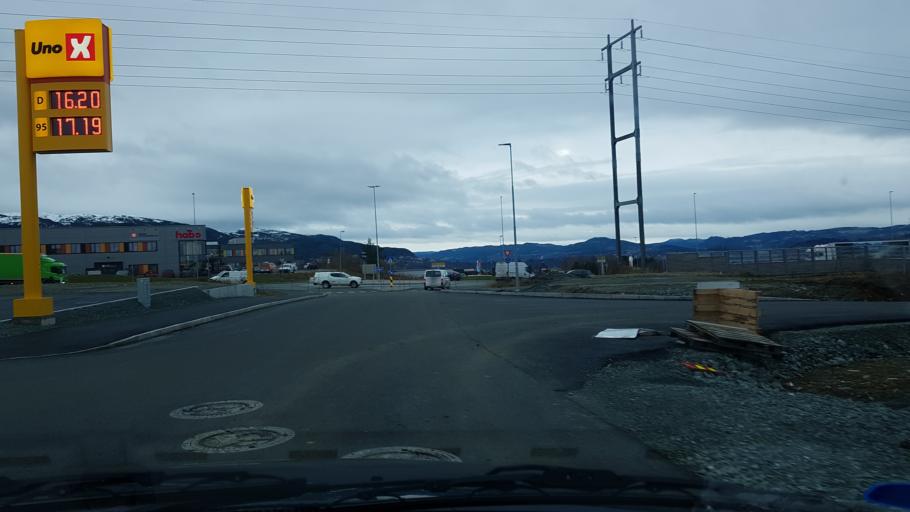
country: NO
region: Sor-Trondelag
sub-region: Melhus
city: Melhus
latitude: 63.3341
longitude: 10.3597
